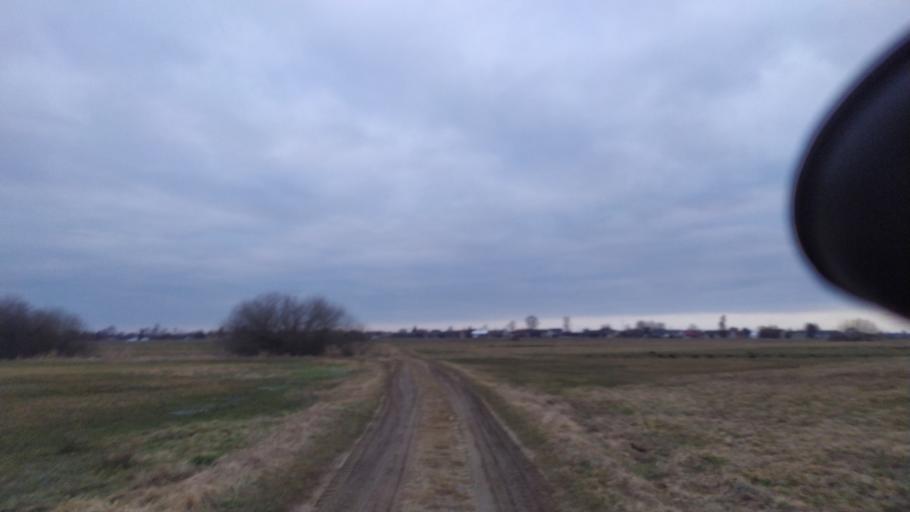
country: PL
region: Lublin Voivodeship
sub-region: Powiat lubartowski
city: Abramow
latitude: 51.4349
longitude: 22.2940
